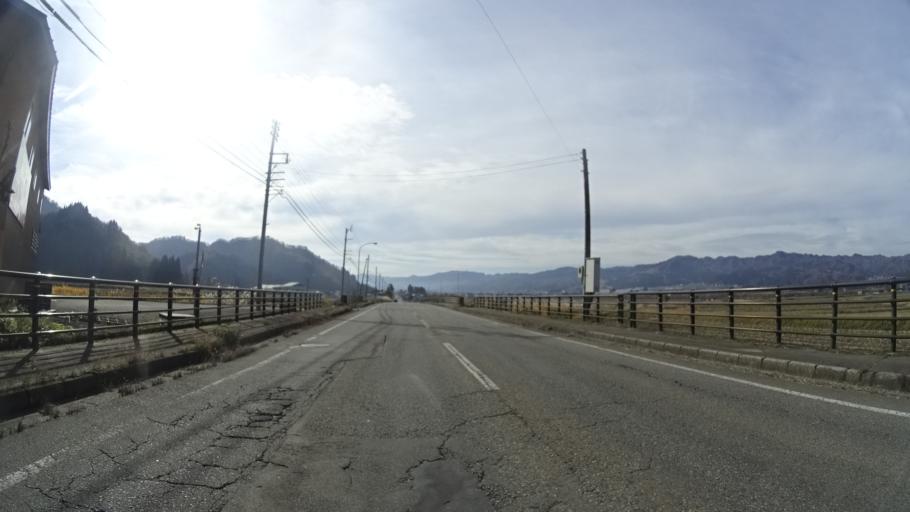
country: JP
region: Niigata
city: Muikamachi
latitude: 37.1282
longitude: 138.9364
